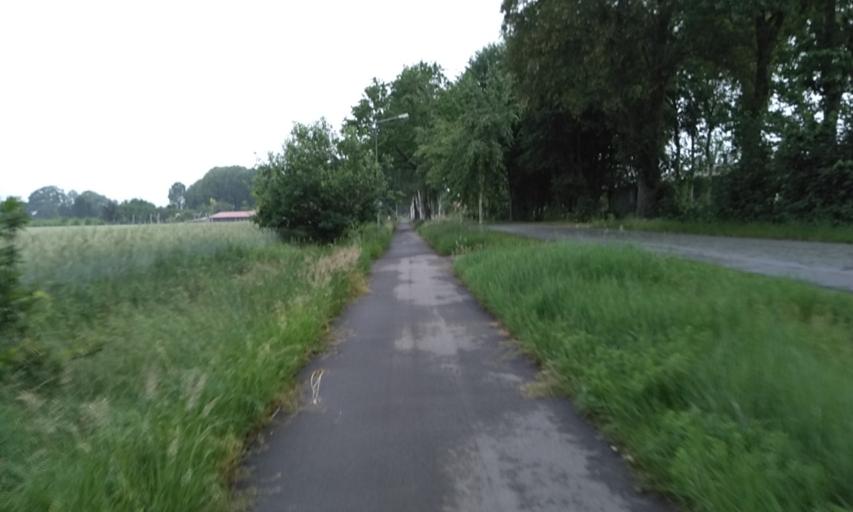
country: DE
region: Lower Saxony
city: Deinste
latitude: 53.5175
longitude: 9.4460
